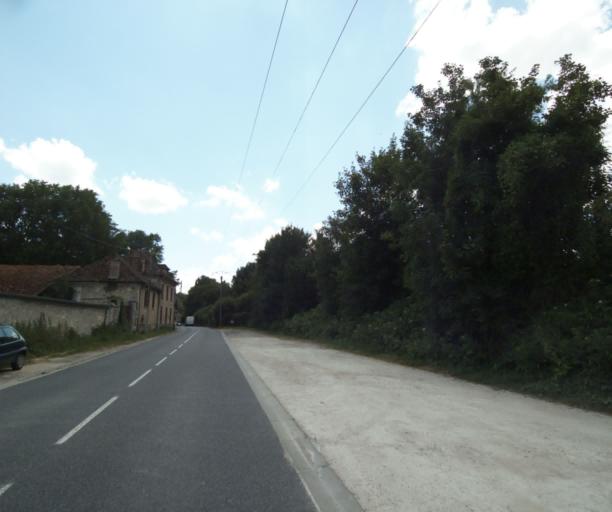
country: FR
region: Ile-de-France
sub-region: Departement de Seine-et-Marne
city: Hericy
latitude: 48.4633
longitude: 2.7730
